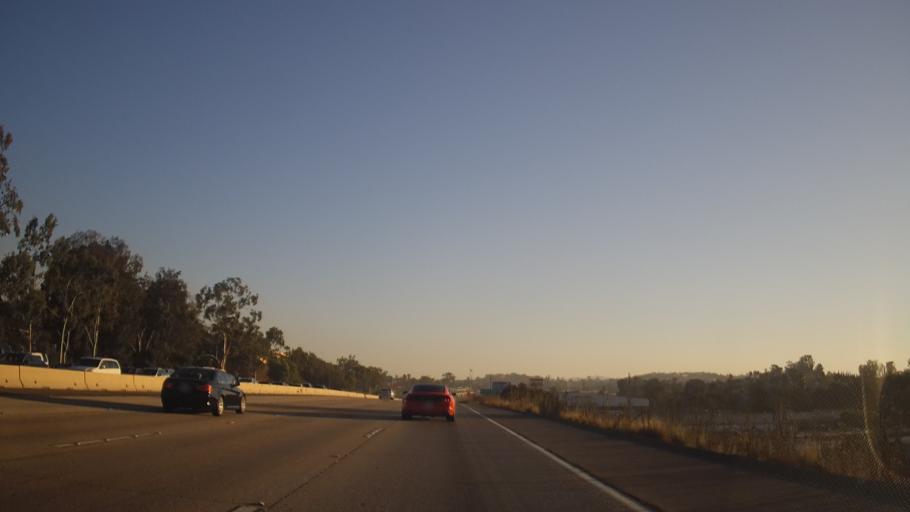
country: US
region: California
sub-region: San Diego County
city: Lemon Grove
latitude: 32.7347
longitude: -117.0576
